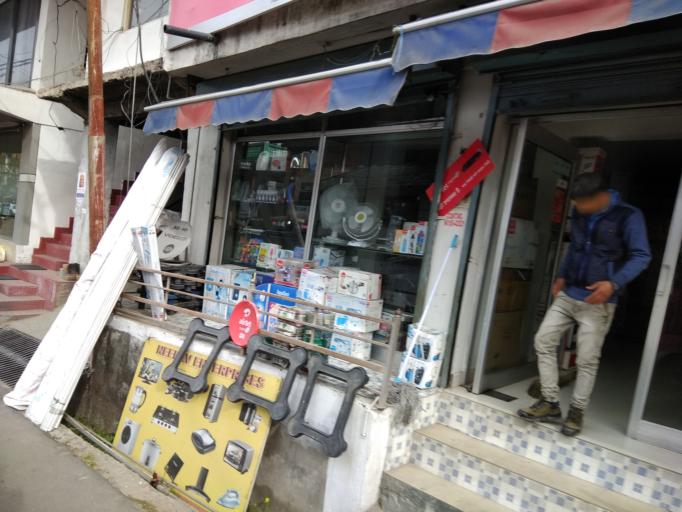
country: IN
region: Himachal Pradesh
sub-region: Kangra
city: Dharmsala
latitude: 32.1880
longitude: 76.3607
